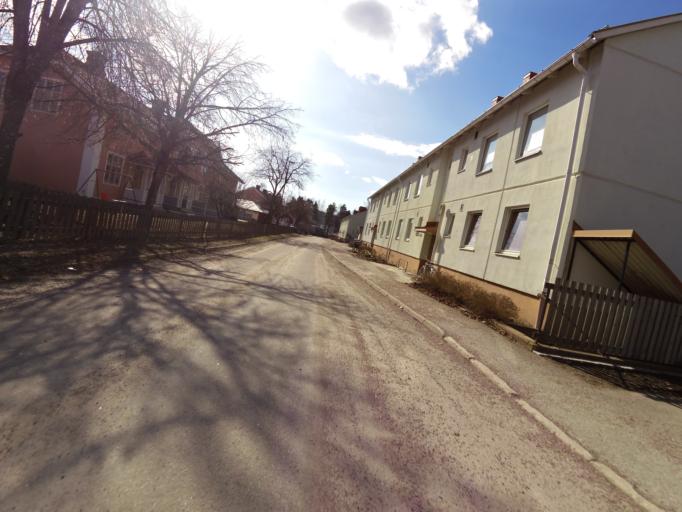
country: SE
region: Gaevleborg
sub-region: Hofors Kommun
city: Hofors
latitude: 60.5442
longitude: 16.2909
